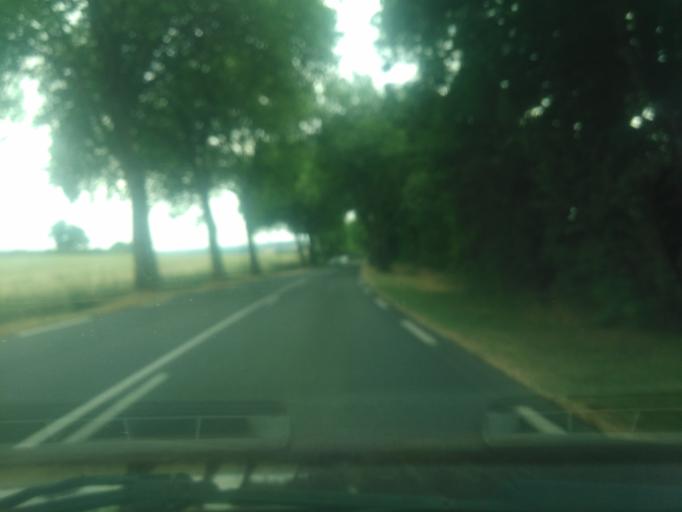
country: FR
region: Poitou-Charentes
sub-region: Departement des Deux-Sevres
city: Moncoutant
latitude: 46.6439
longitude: -0.6188
